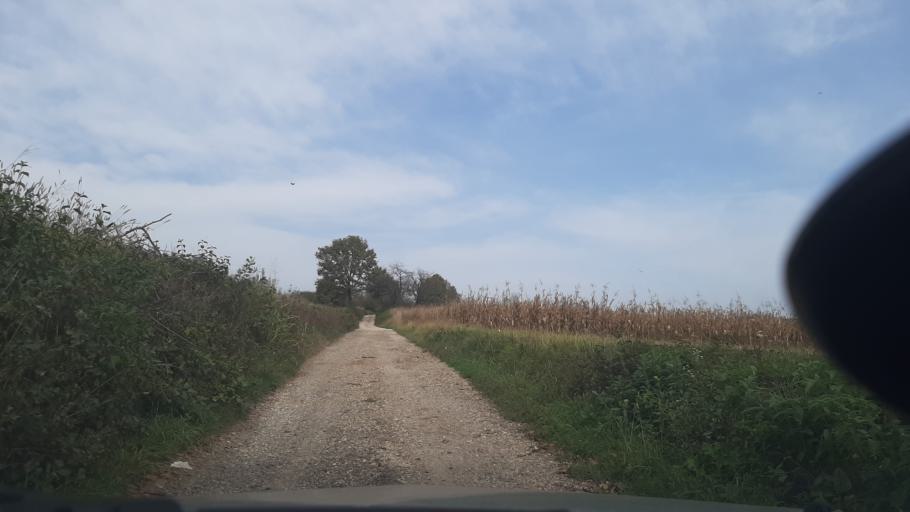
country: BA
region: Republika Srpska
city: Maglajani
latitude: 44.8732
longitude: 17.4713
